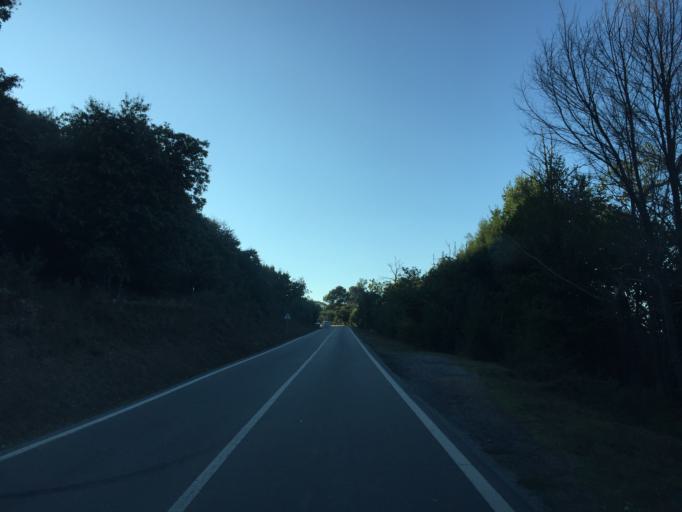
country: PT
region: Portalegre
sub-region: Castelo de Vide
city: Castelo de Vide
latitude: 39.4013
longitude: -7.4342
